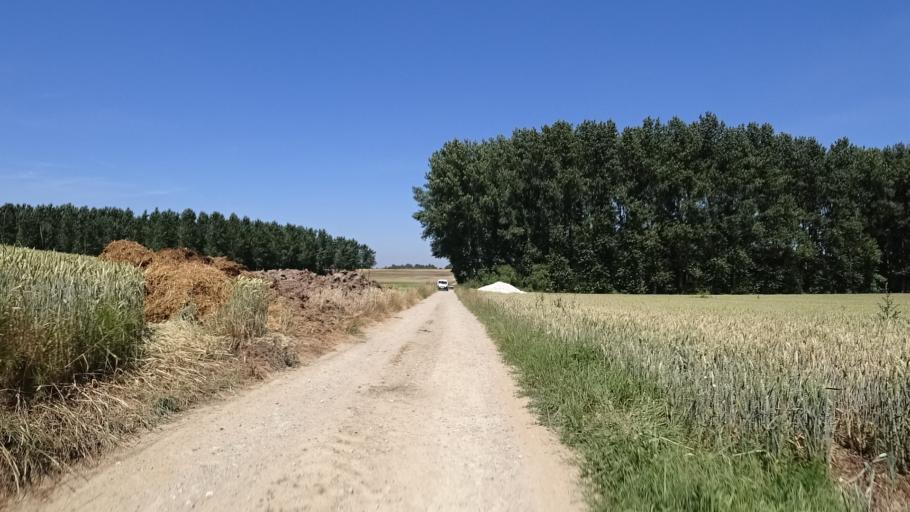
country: BE
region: Wallonia
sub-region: Province du Brabant Wallon
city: Jodoigne
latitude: 50.7026
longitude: 4.8605
